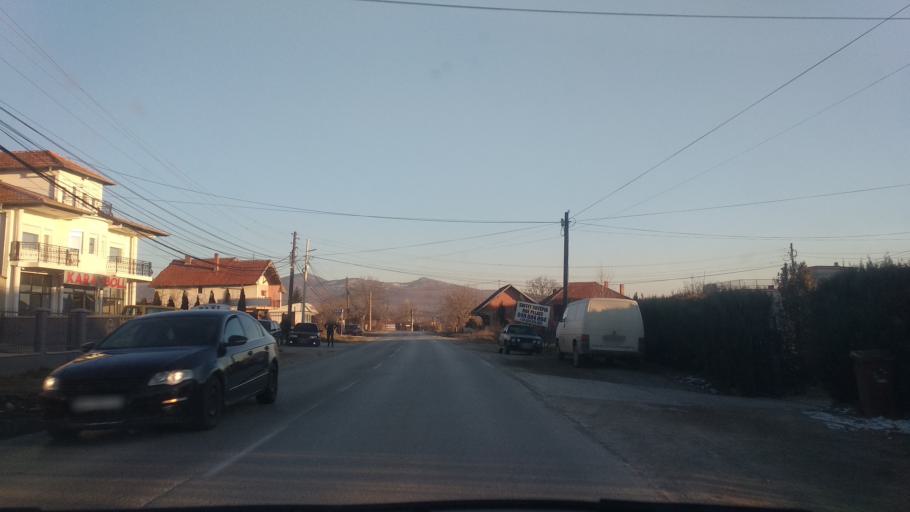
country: XK
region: Pristina
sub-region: Komuna e Prishtines
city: Pristina
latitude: 42.6078
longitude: 21.1820
